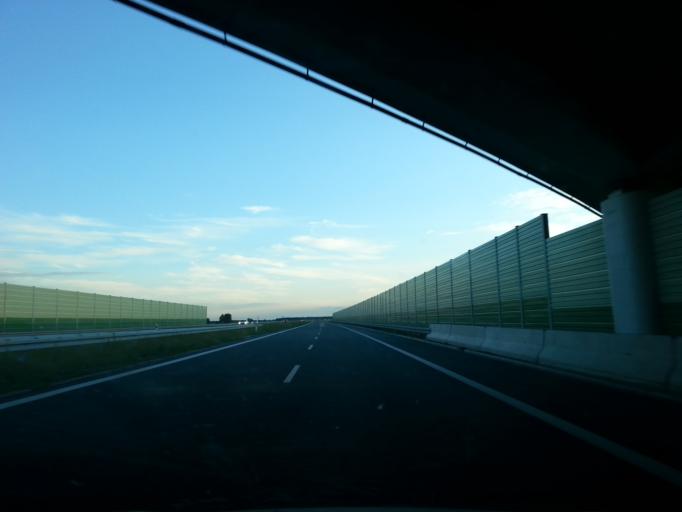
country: PL
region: Greater Poland Voivodeship
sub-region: Powiat kepinski
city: Bralin
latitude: 51.3079
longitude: 17.9235
